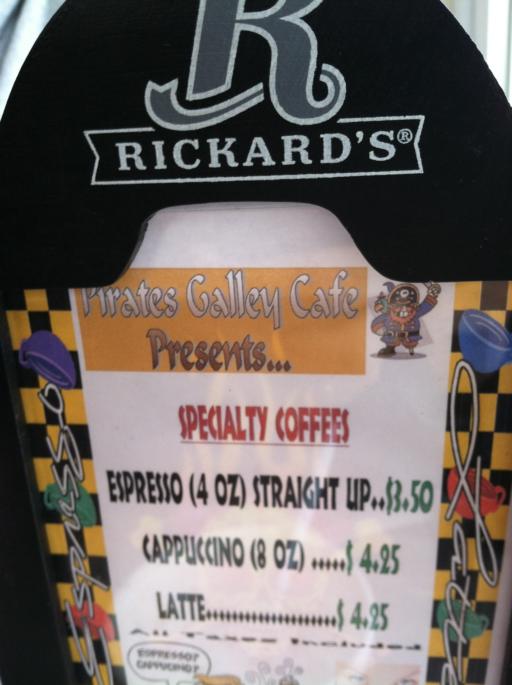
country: CA
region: Prince Edward Island
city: Souris
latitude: 46.4525
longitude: -61.9717
